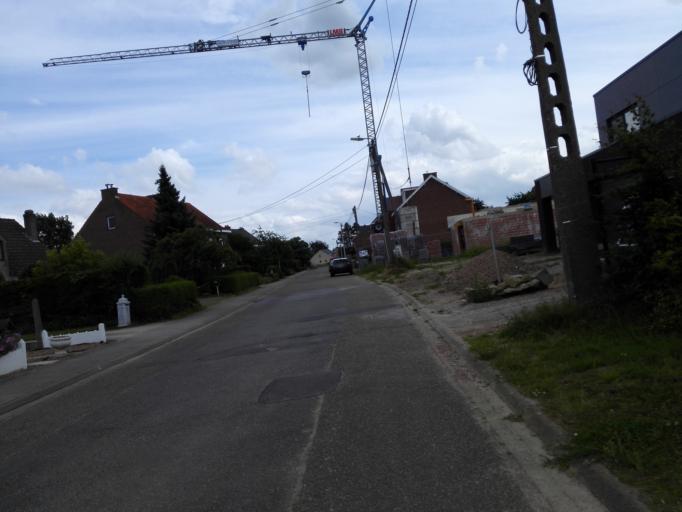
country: BE
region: Flanders
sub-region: Provincie Vlaams-Brabant
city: Bierbeek
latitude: 50.8494
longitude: 4.7865
